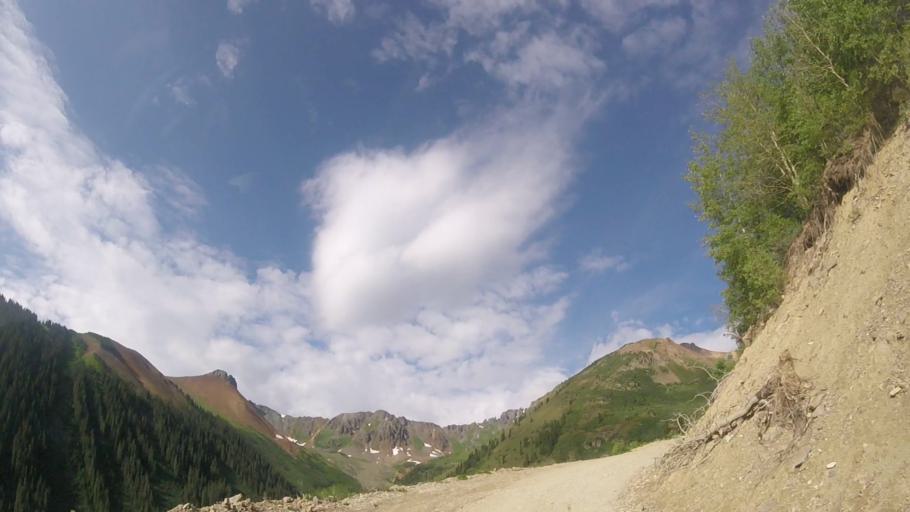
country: US
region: Colorado
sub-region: San Miguel County
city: Telluride
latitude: 37.8459
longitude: -107.7642
